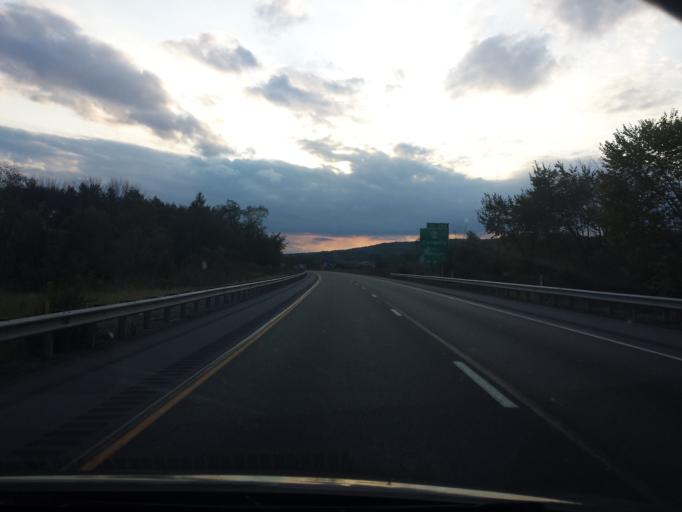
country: US
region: Pennsylvania
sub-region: Montour County
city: Danville
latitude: 41.0002
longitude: -76.6282
